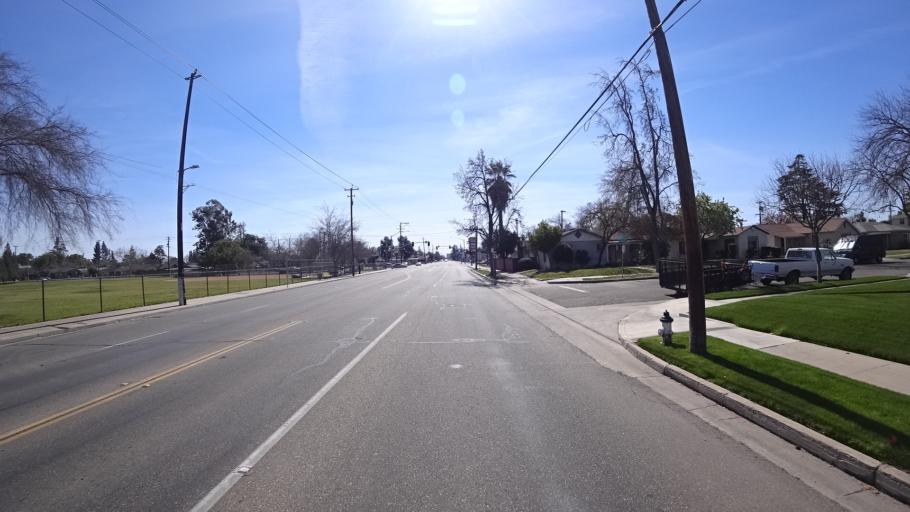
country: US
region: California
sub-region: Fresno County
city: Fresno
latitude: 36.7661
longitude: -119.8087
